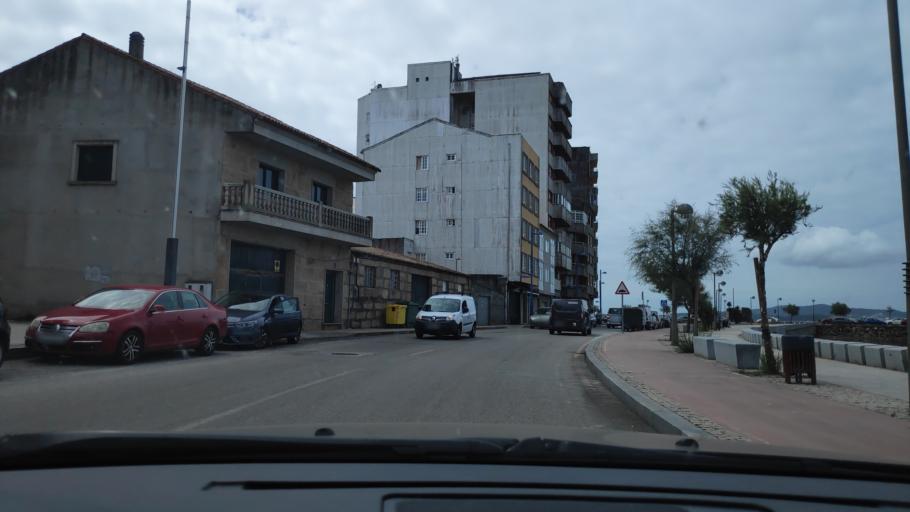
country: ES
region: Galicia
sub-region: Provincia de Pontevedra
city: Cambados
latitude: 42.5201
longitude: -8.8163
